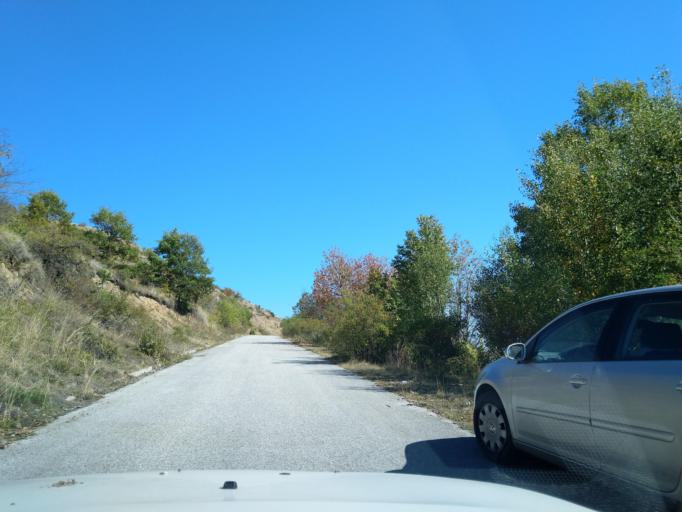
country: RS
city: Sokolovica
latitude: 43.2542
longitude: 20.3379
